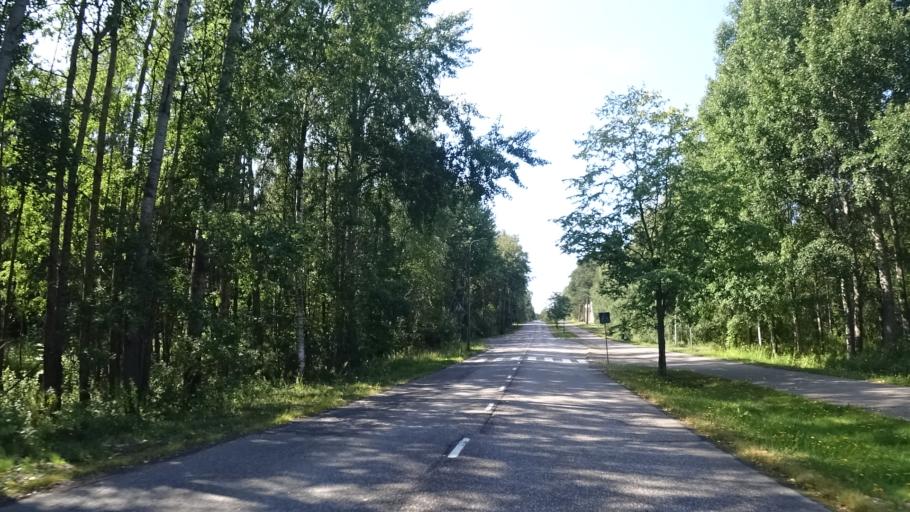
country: FI
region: Kymenlaakso
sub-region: Kotka-Hamina
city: Karhula
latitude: 60.4982
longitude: 26.9680
